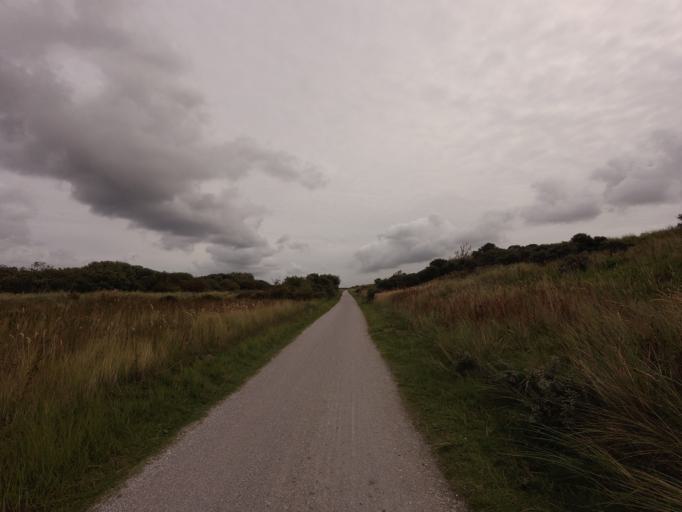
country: NL
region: Friesland
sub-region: Gemeente Ameland
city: Hollum
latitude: 53.4583
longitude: 5.6714
